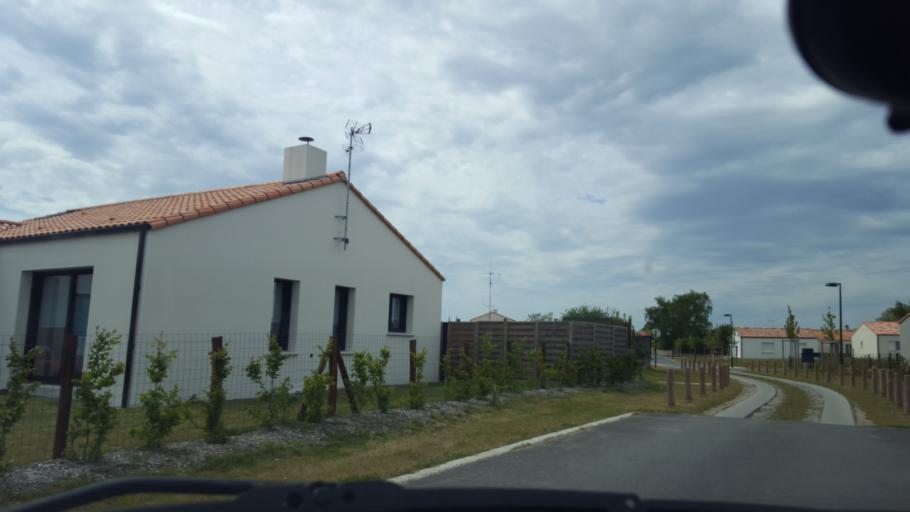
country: FR
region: Pays de la Loire
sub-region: Departement de la Loire-Atlantique
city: Machecoul
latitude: 46.9888
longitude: -1.8007
